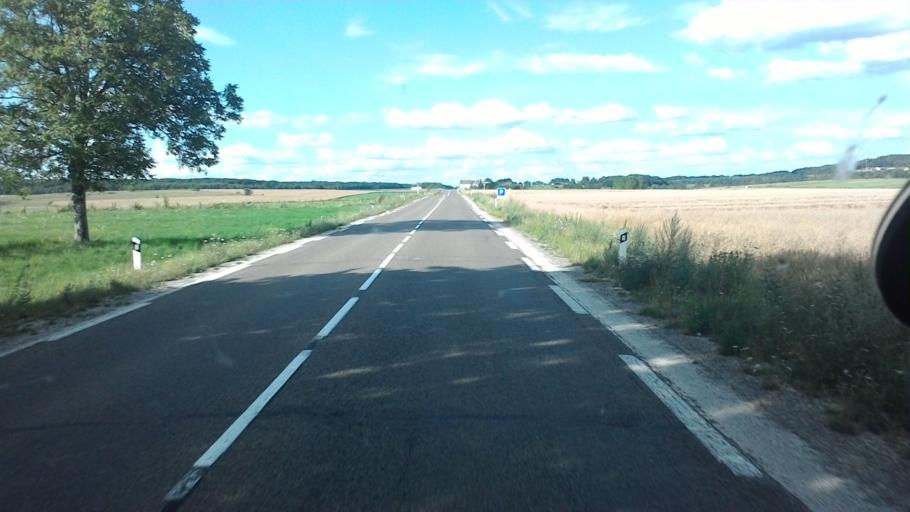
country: FR
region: Franche-Comte
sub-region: Departement de la Haute-Saone
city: Luxeuil-les-Bains
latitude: 47.7217
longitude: 6.3057
